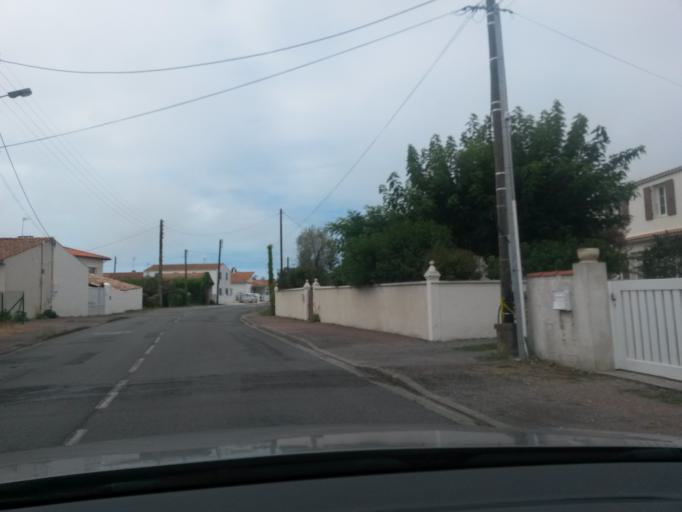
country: FR
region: Poitou-Charentes
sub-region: Departement de la Charente-Maritime
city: Saint-Trojan-les-Bains
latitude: 45.8733
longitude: -1.2094
